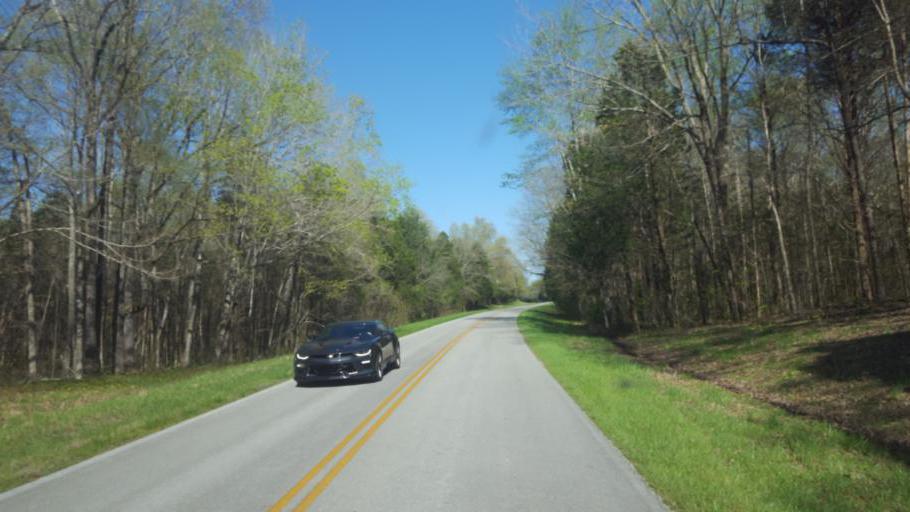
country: US
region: Kentucky
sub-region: Edmonson County
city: Brownsville
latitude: 37.1597
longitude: -86.1495
